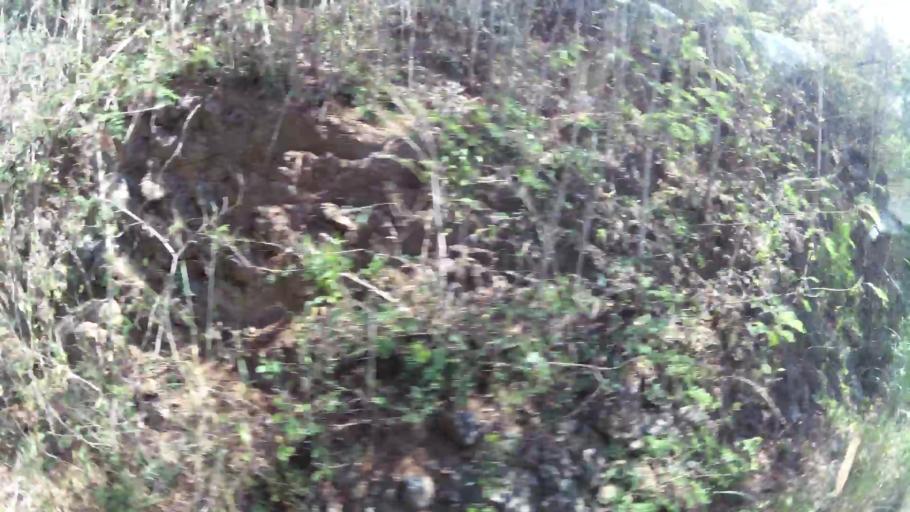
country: VG
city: Tortola
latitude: 18.4301
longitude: -64.5998
